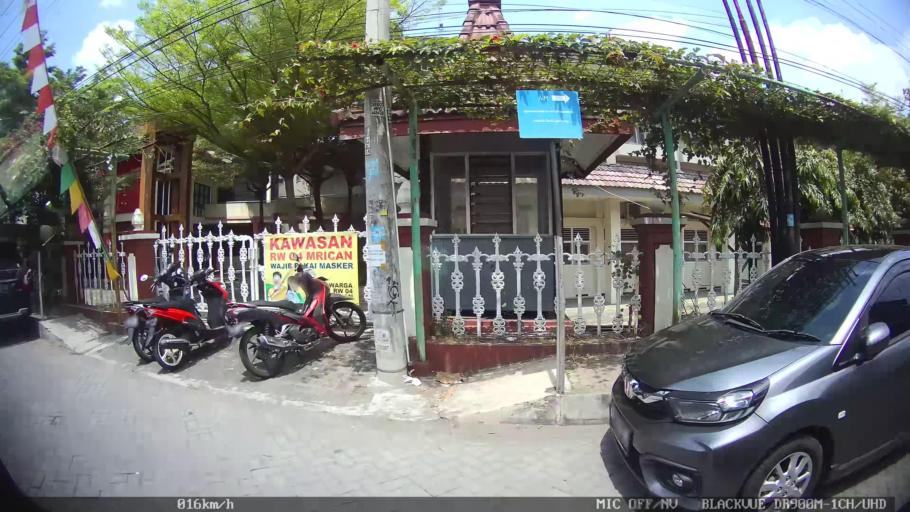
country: ID
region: Daerah Istimewa Yogyakarta
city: Yogyakarta
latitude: -7.7733
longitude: 110.3881
